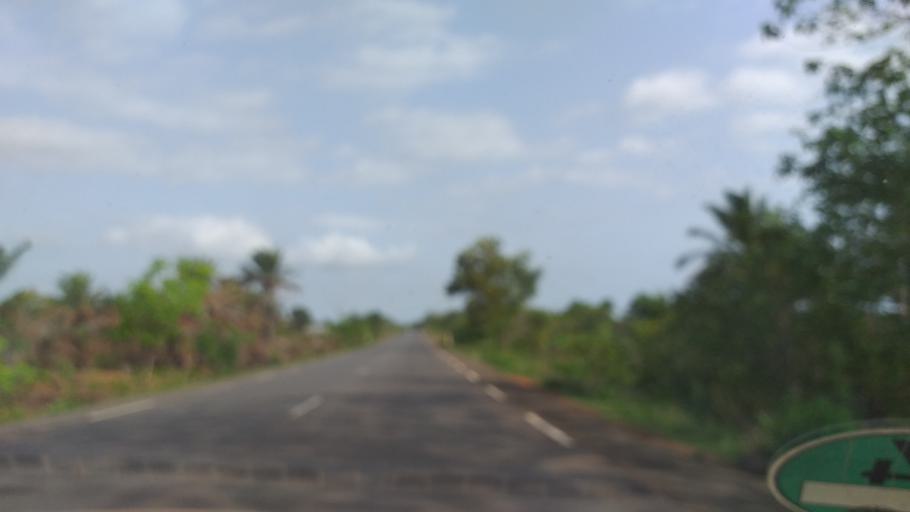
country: GN
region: Boke
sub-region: Boke Prefecture
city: Sangueya
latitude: 10.4423
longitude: -14.4034
